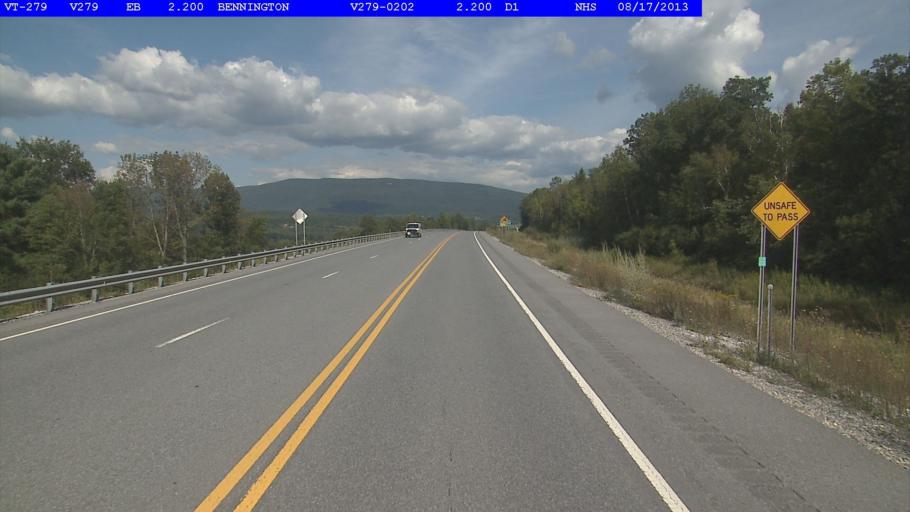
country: US
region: Vermont
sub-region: Bennington County
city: North Bennington
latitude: 42.9063
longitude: -73.2386
